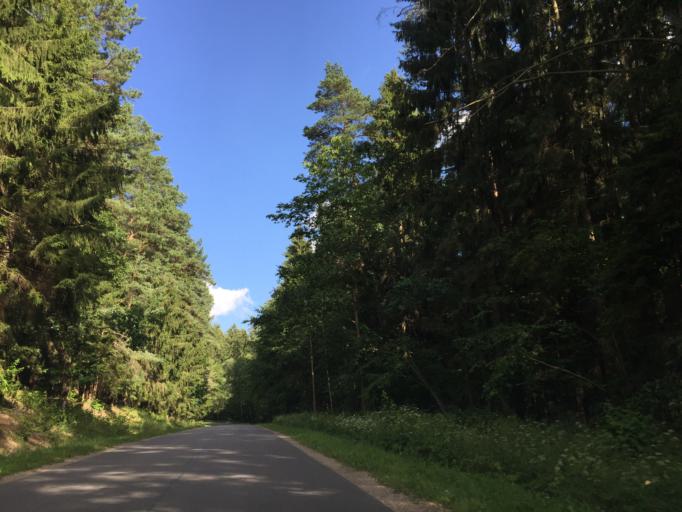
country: PL
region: Podlasie
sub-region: Suwalki
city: Suwalki
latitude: 54.1467
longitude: 23.0669
